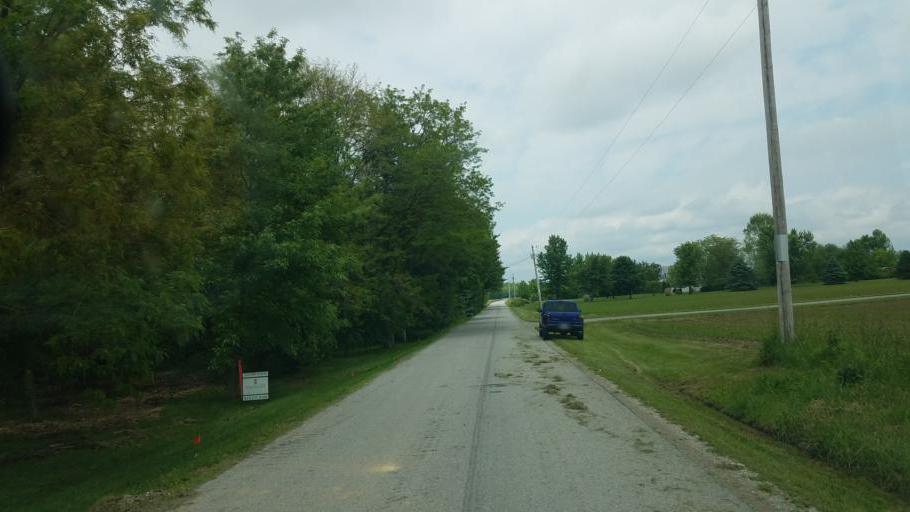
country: US
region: Ohio
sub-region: Marion County
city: Prospect
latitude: 40.3594
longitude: -83.1813
